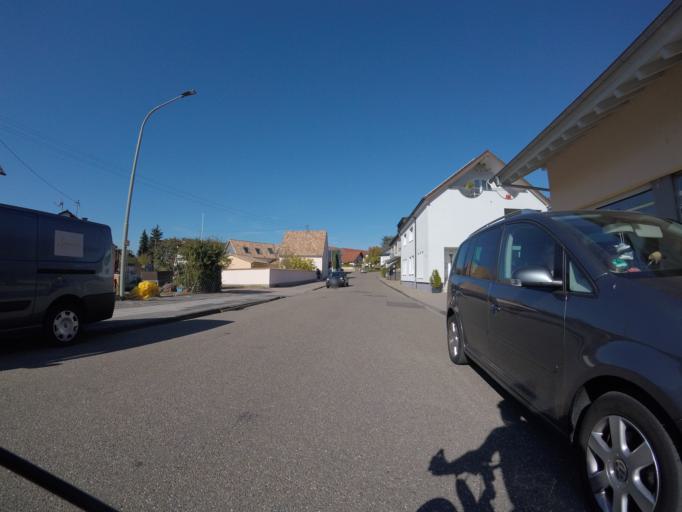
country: DE
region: Rheinland-Pfalz
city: Germersheim
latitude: 49.2635
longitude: 8.4018
